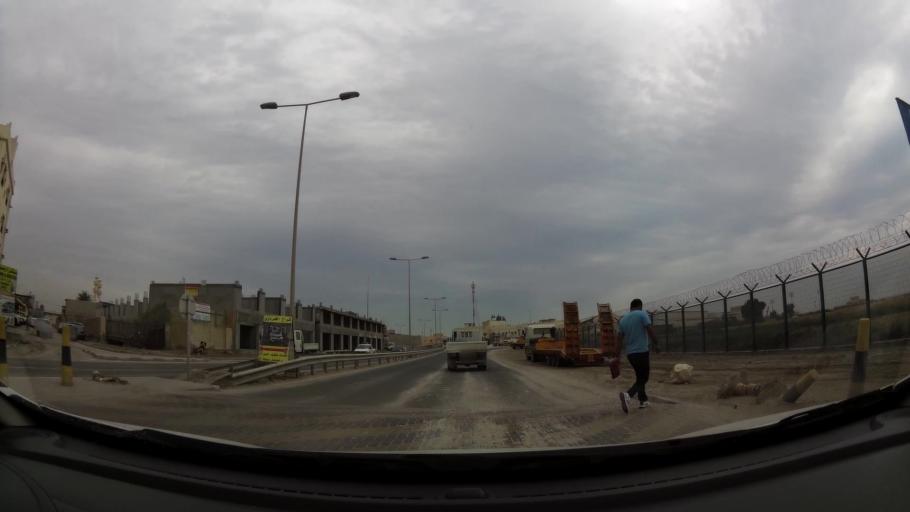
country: BH
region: Northern
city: Sitrah
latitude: 26.1523
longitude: 50.6206
